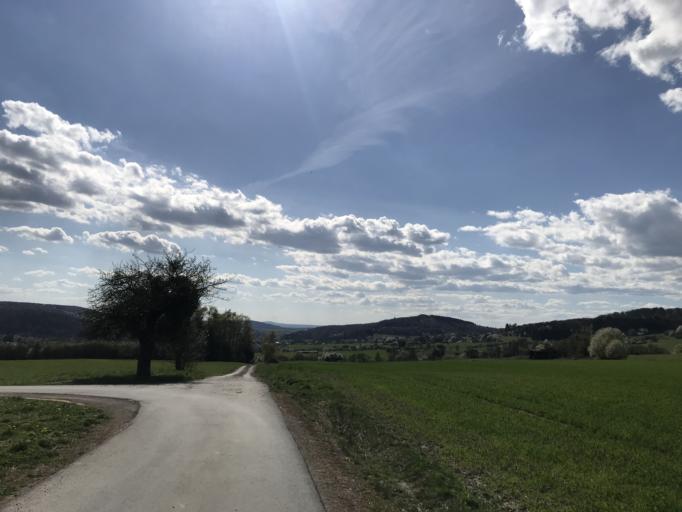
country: DE
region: Hesse
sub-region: Regierungsbezirk Giessen
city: Rabenau
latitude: 50.6906
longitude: 8.8356
